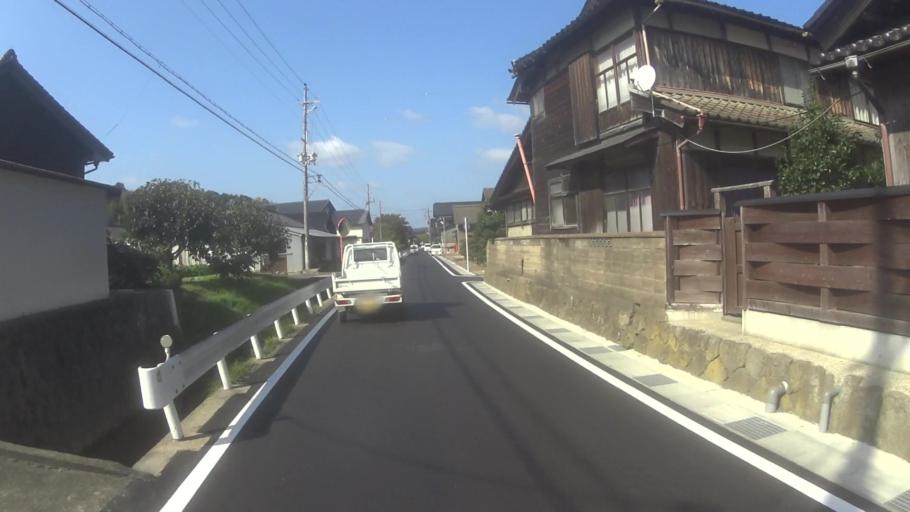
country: JP
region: Kyoto
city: Miyazu
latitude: 35.6782
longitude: 135.0527
